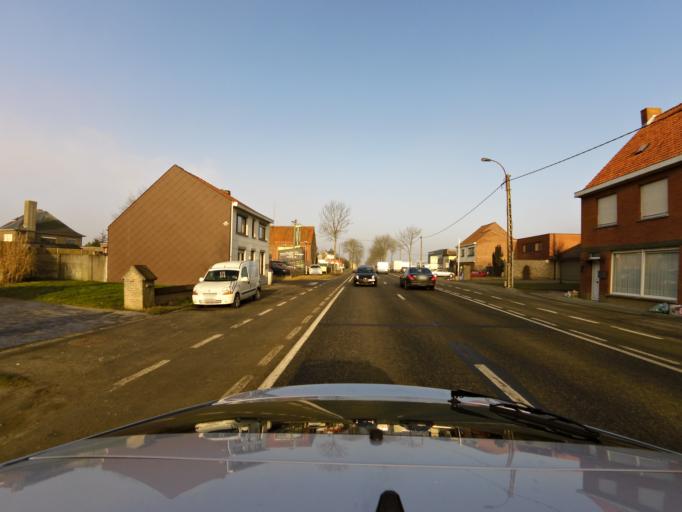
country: BE
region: Flanders
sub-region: Provincie West-Vlaanderen
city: Ichtegem
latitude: 51.0910
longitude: 3.0487
